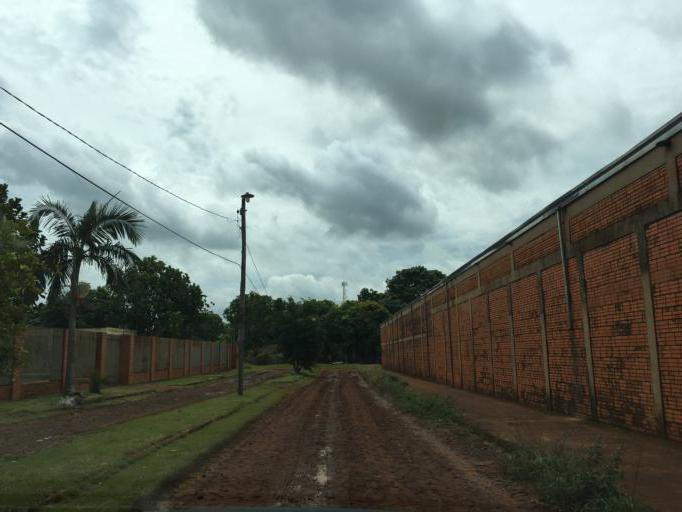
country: PY
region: Alto Parana
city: Ciudad del Este
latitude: -25.4211
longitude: -54.6375
